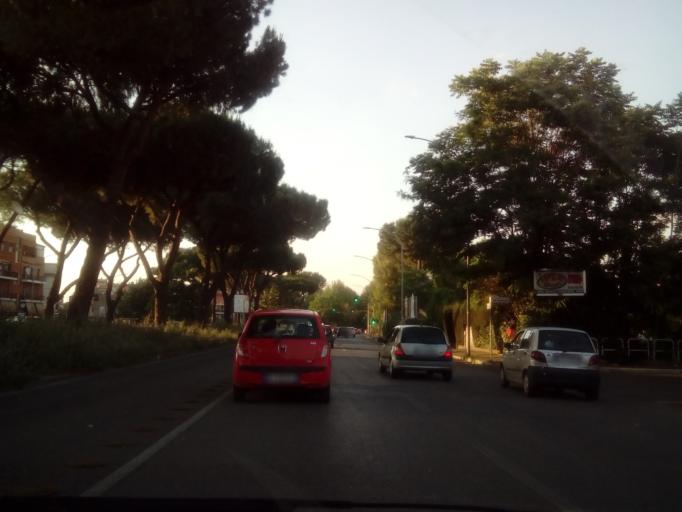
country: IT
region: Latium
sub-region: Citta metropolitana di Roma Capitale
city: Rome
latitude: 41.8879
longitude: 12.5738
